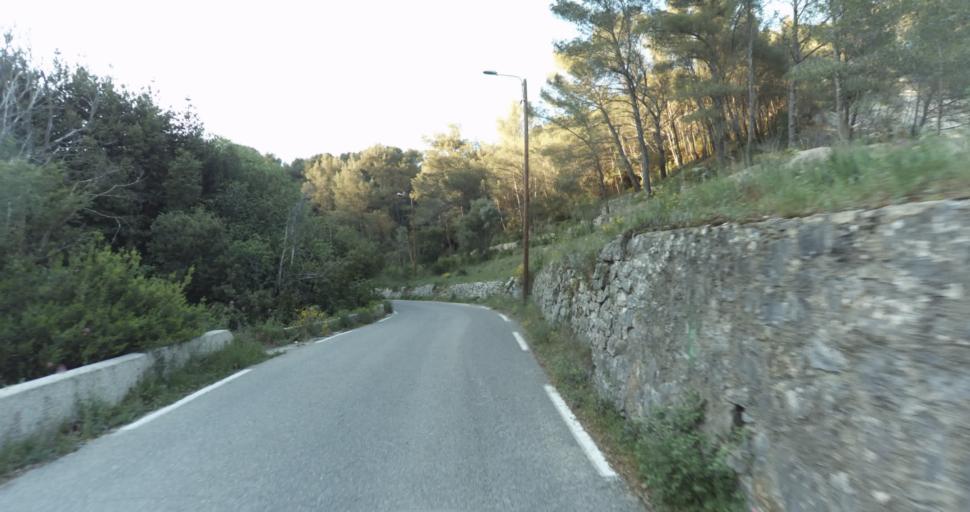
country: FR
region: Provence-Alpes-Cote d'Azur
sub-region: Departement du Var
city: Le Revest-les-Eaux
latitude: 43.1721
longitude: 5.9334
